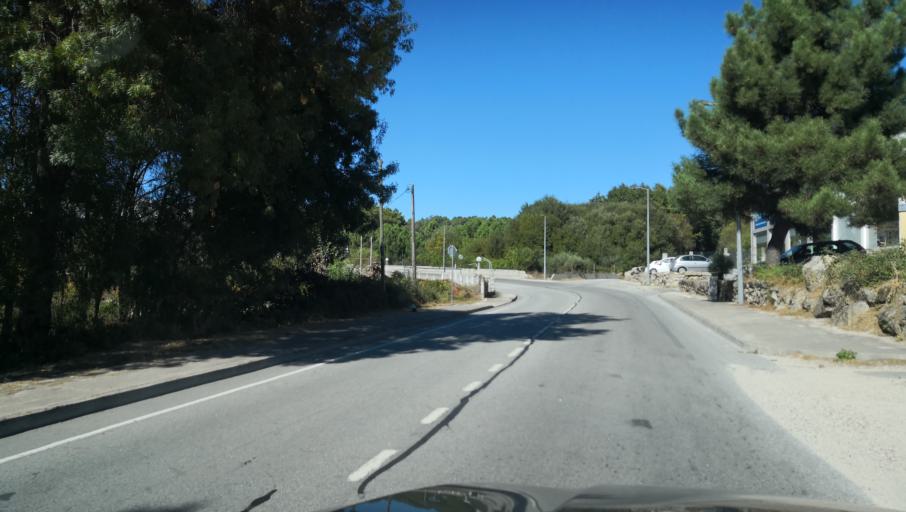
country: PT
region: Vila Real
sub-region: Valpacos
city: Valpacos
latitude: 41.6284
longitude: -7.3128
